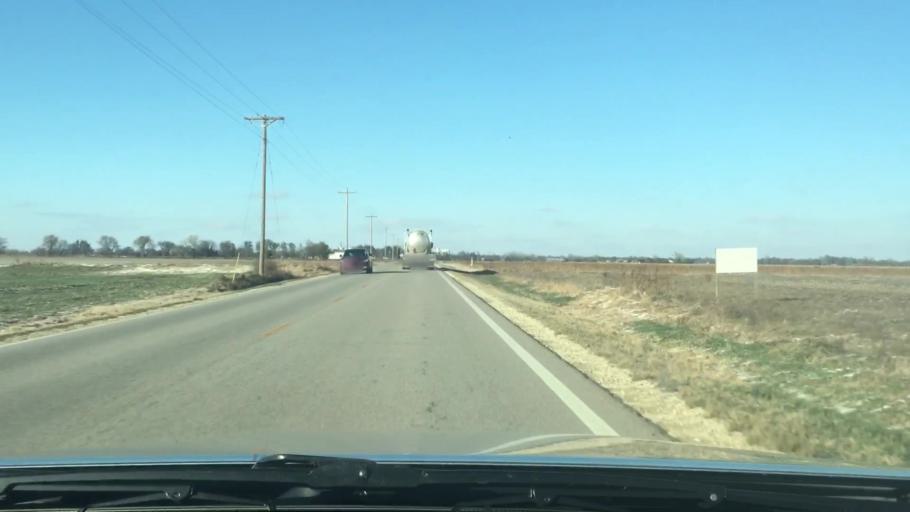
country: US
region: Kansas
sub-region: Rice County
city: Sterling
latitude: 38.1801
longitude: -98.2069
